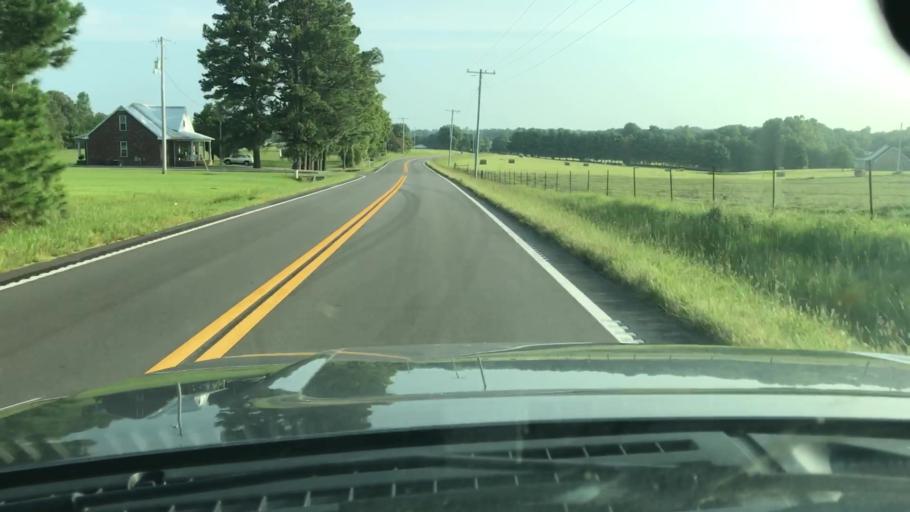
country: US
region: Tennessee
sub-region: Sumner County
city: Portland
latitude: 36.5446
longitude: -86.4100
